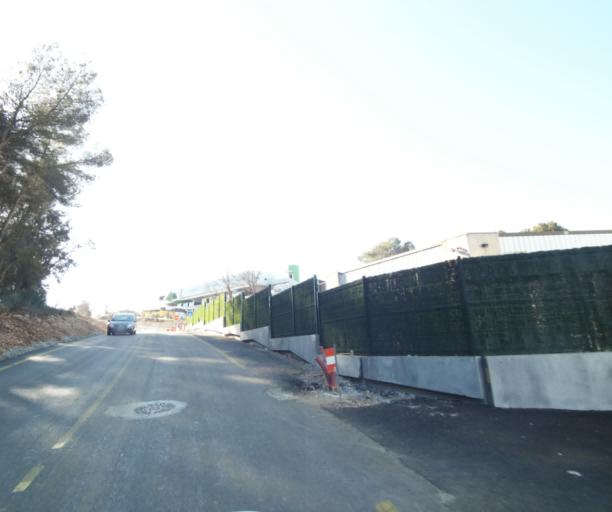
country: FR
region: Provence-Alpes-Cote d'Azur
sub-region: Departement des Alpes-Maritimes
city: Biot
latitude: 43.6087
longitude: 7.0747
